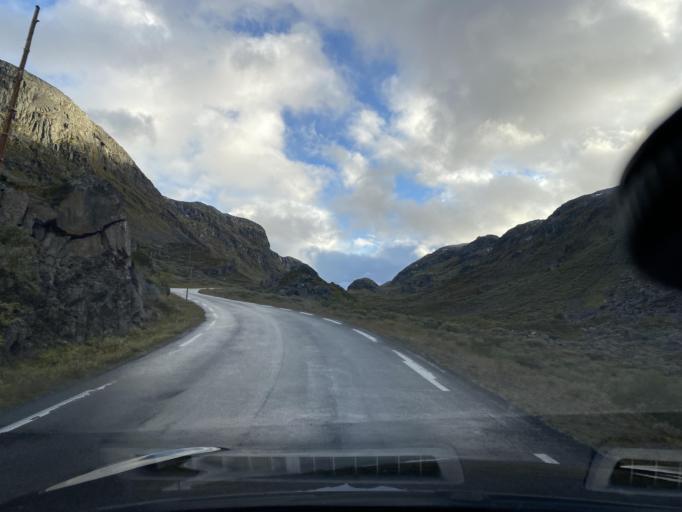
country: NO
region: Oppland
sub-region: Skjak
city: Bismo
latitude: 61.6116
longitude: 8.0411
